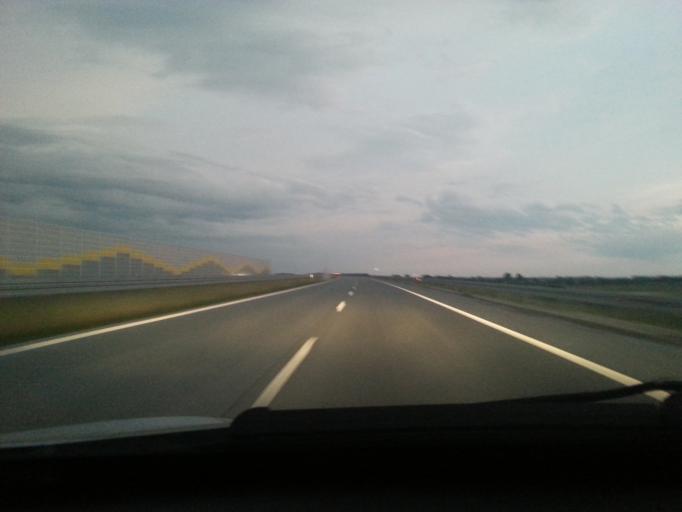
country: PL
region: Lodz Voivodeship
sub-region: Powiat sieradzki
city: Sieradz
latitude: 51.5888
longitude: 18.8103
